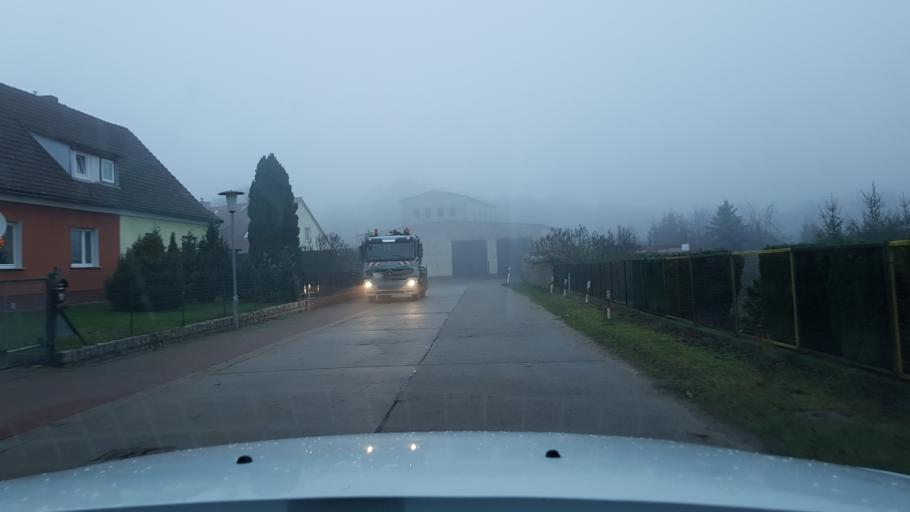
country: DE
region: Brandenburg
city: Mescherin
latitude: 53.2688
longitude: 14.4314
